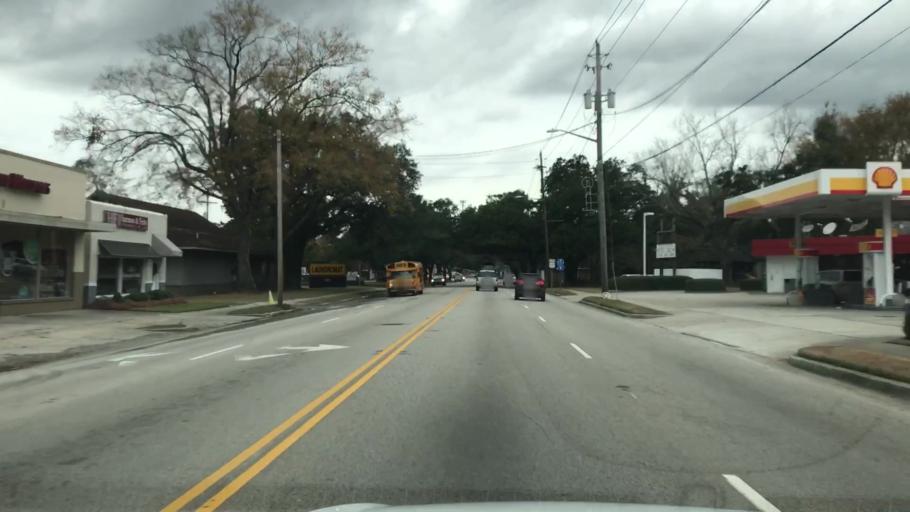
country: US
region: South Carolina
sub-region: Georgetown County
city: Georgetown
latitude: 33.3738
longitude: -79.2833
